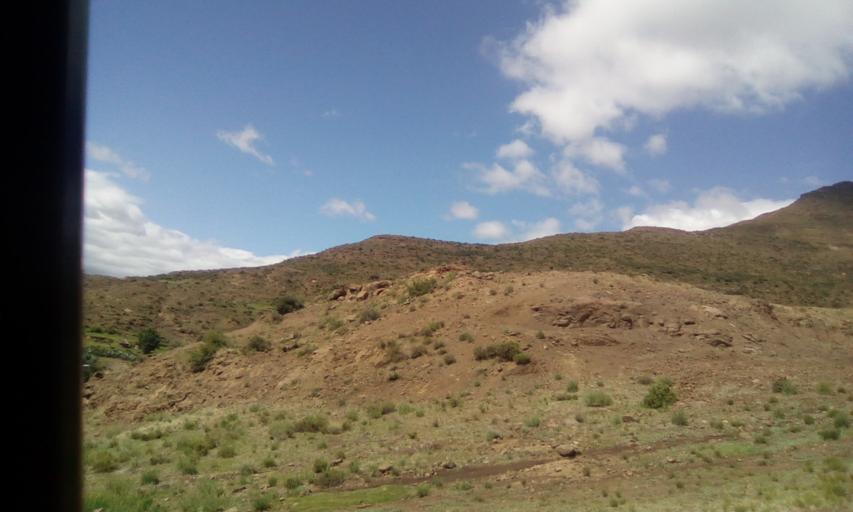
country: LS
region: Maseru
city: Nako
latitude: -29.6573
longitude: 27.7839
